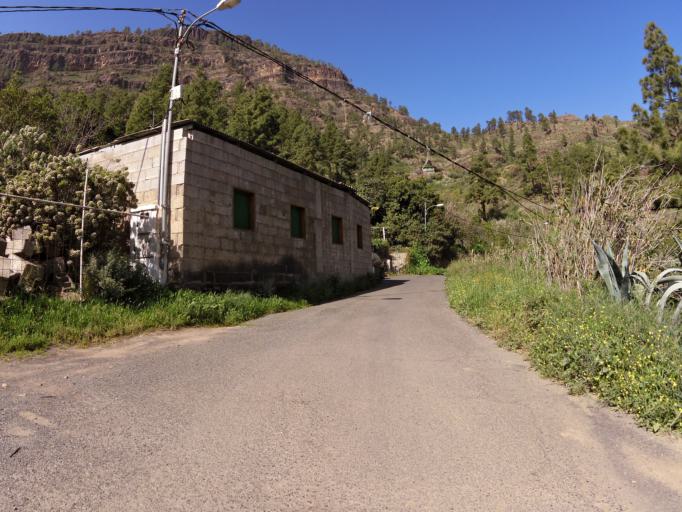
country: ES
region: Canary Islands
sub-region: Provincia de Las Palmas
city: Mogan
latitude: 27.8971
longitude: -15.6814
